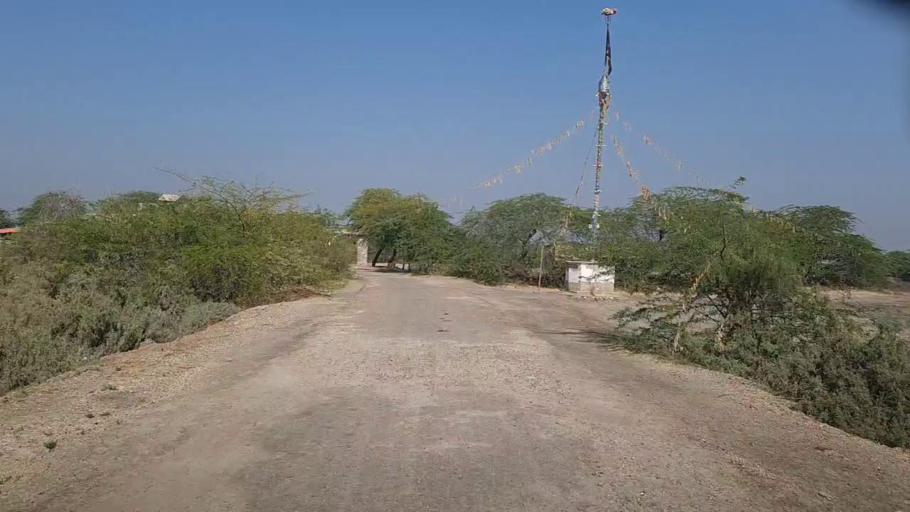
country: PK
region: Sindh
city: Bozdar
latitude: 27.2528
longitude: 68.5978
